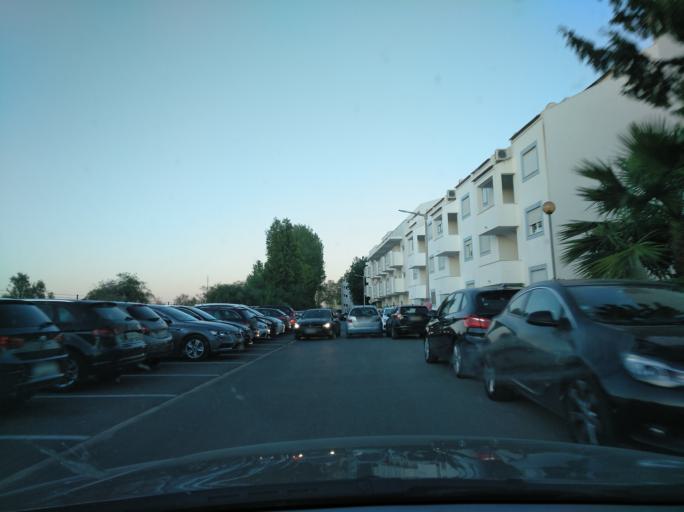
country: PT
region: Faro
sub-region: Tavira
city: Tavira
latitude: 37.1337
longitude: -7.6073
